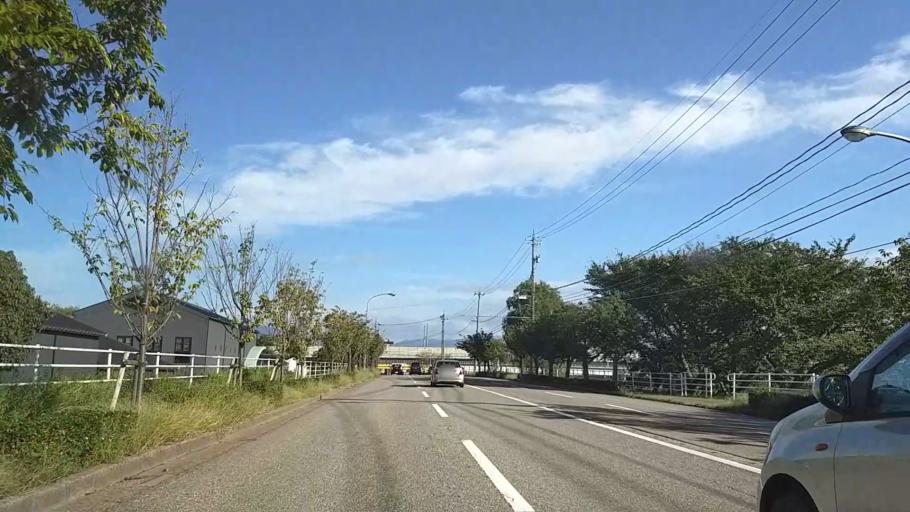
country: JP
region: Ishikawa
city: Kanazawa-shi
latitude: 36.5687
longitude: 136.6378
